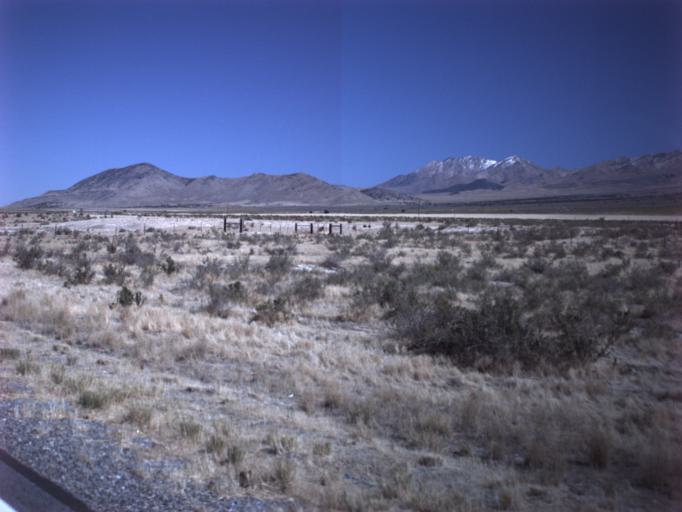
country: US
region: Utah
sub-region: Tooele County
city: Grantsville
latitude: 40.4836
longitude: -112.7455
